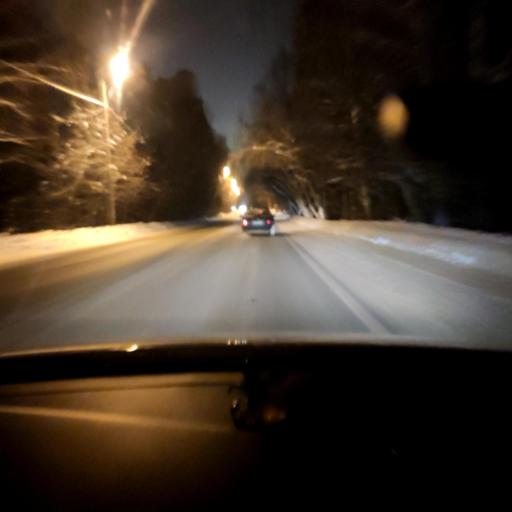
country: RU
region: Tatarstan
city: Osinovo
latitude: 55.8306
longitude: 48.8924
